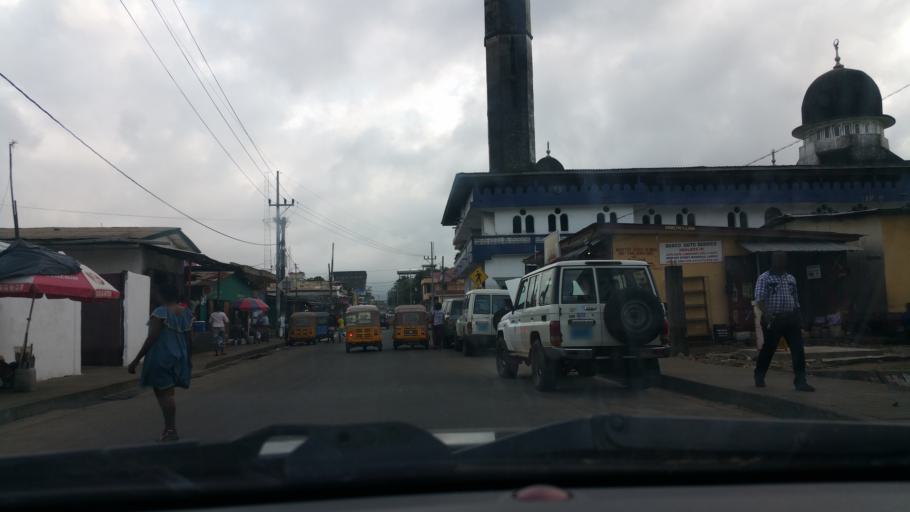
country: LR
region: Montserrado
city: Monrovia
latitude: 6.3125
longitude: -10.8107
